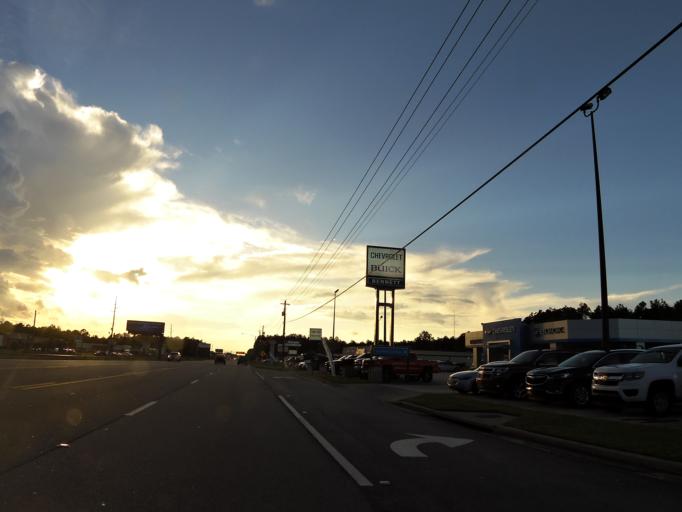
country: US
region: Georgia
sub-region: Camden County
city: St Marys
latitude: 30.7808
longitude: -81.6271
